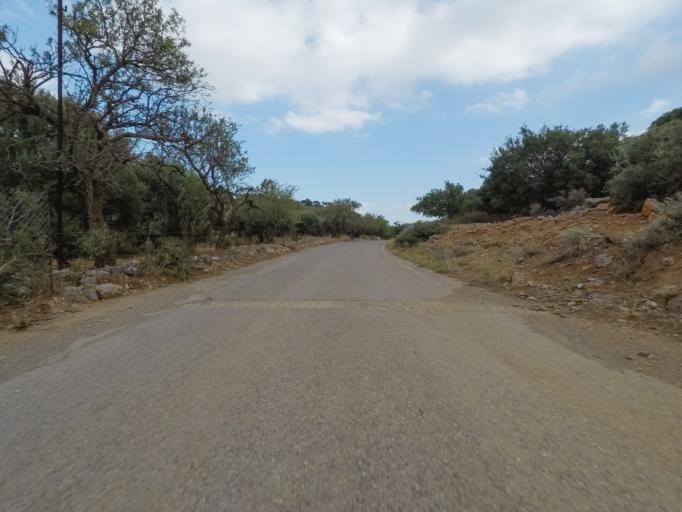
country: GR
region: Crete
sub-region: Nomos Lasithiou
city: Kritsa
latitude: 35.1697
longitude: 25.6544
